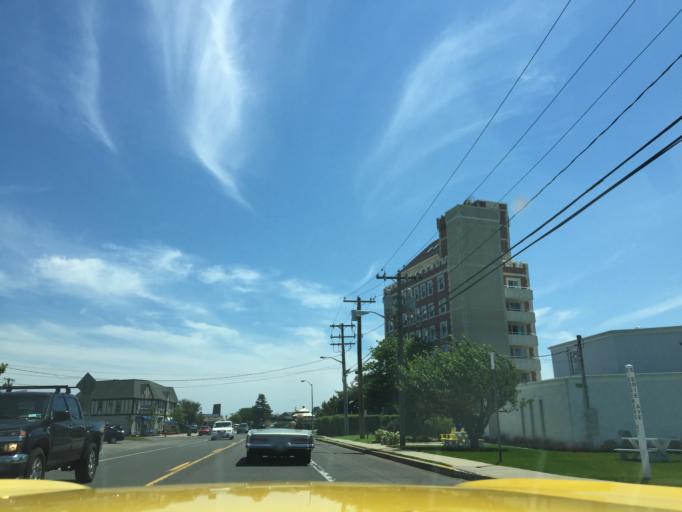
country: US
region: New York
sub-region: Suffolk County
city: Montauk
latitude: 41.0365
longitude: -71.9448
